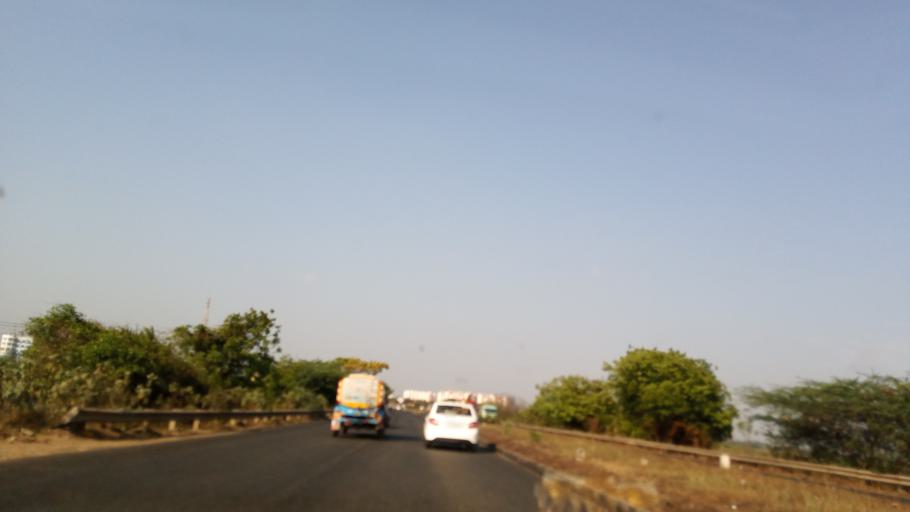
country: IN
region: Tamil Nadu
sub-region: Kancheepuram
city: Nandambakkam
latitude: 13.0191
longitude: 80.0119
